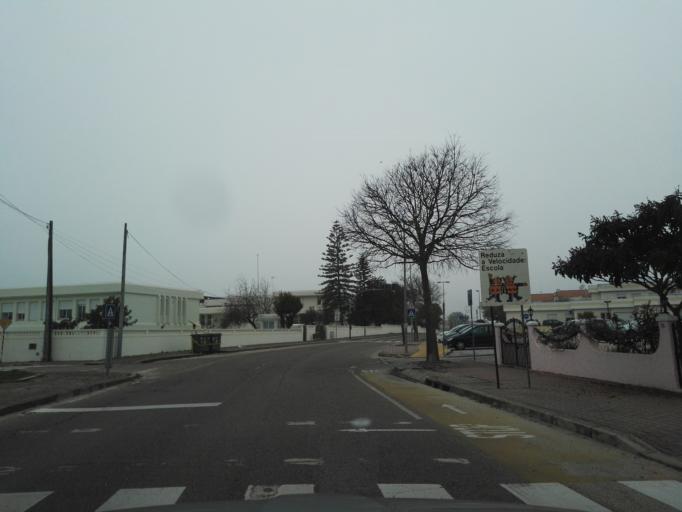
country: PT
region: Evora
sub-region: Vendas Novas
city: Vendas Novas
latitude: 38.6744
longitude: -8.4541
